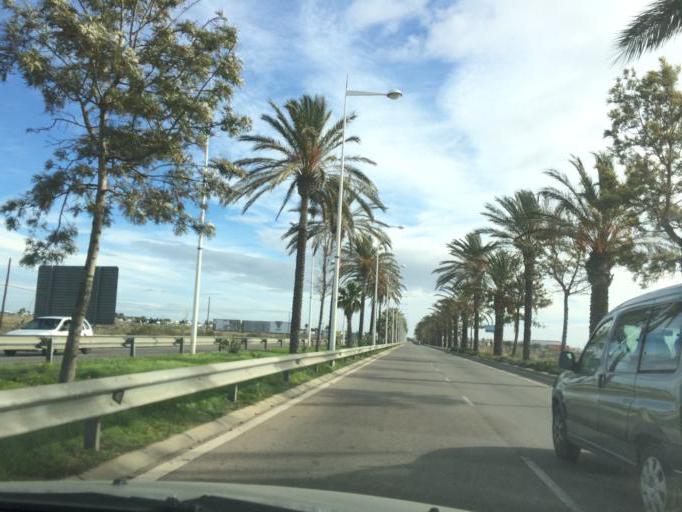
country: ES
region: Andalusia
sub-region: Provincia de Almeria
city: Retamar
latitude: 36.8521
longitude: -2.3193
